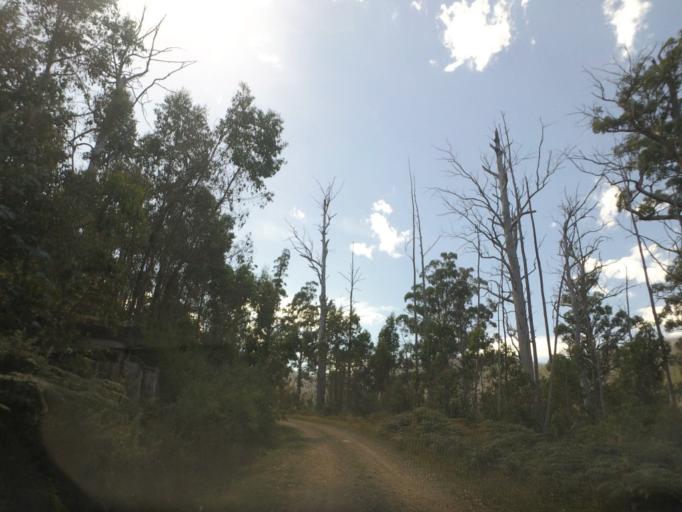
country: AU
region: Victoria
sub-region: Murrindindi
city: Alexandra
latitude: -37.4806
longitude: 145.8402
